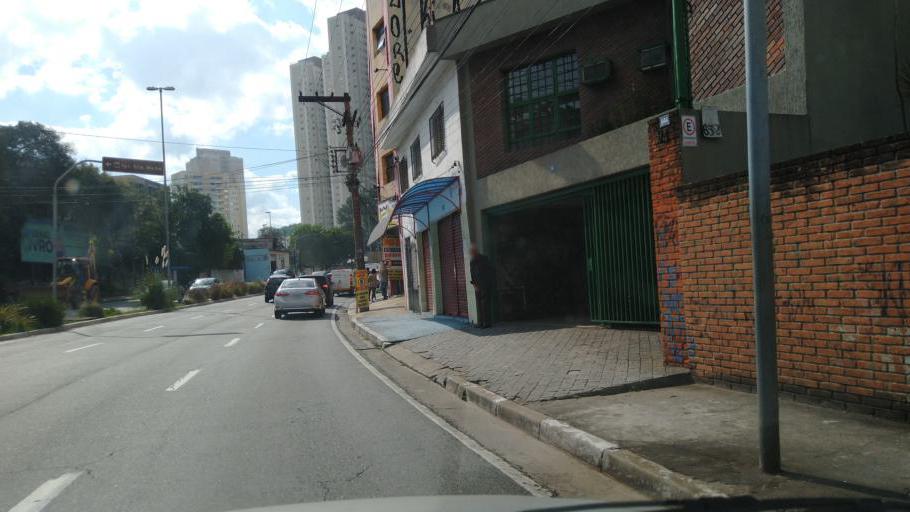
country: BR
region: Sao Paulo
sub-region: Guarulhos
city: Guarulhos
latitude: -23.4675
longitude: -46.5353
